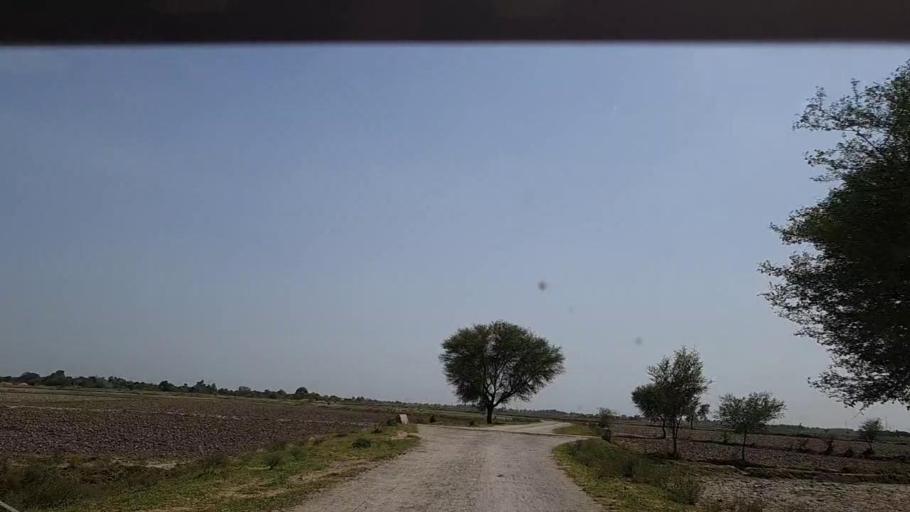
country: PK
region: Sindh
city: Phulji
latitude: 26.9514
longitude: 67.7166
